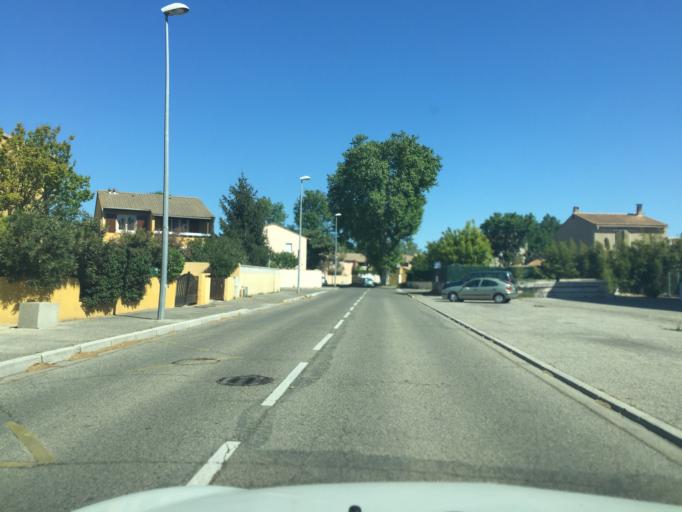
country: FR
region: Provence-Alpes-Cote d'Azur
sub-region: Departement du Vaucluse
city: Le Pontet
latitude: 43.9417
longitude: 4.8385
